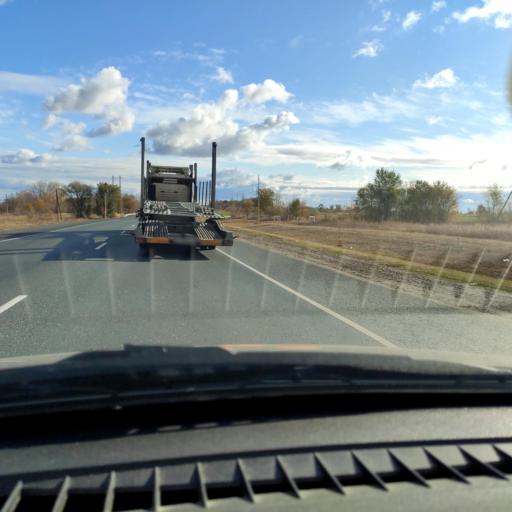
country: RU
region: Samara
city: Varlamovo
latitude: 53.1962
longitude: 48.3132
